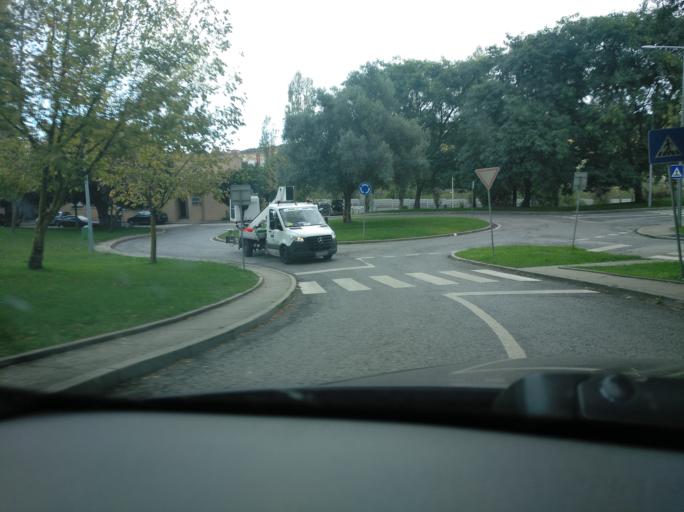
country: PT
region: Lisbon
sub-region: Amadora
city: Amadora
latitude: 38.7350
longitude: -9.2085
